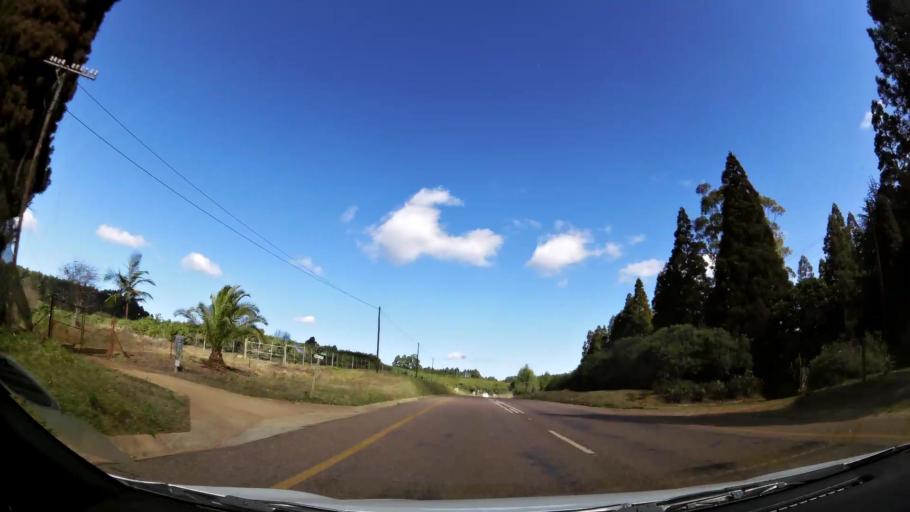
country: ZA
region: Limpopo
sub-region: Capricorn District Municipality
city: Mankoeng
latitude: -23.8986
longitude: 29.9936
